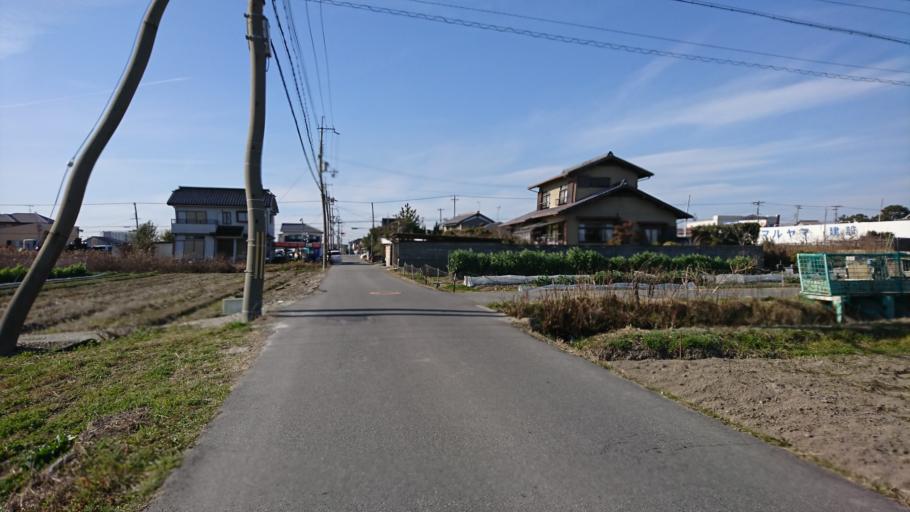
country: JP
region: Hyogo
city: Kakogawacho-honmachi
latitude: 34.7301
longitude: 134.8734
